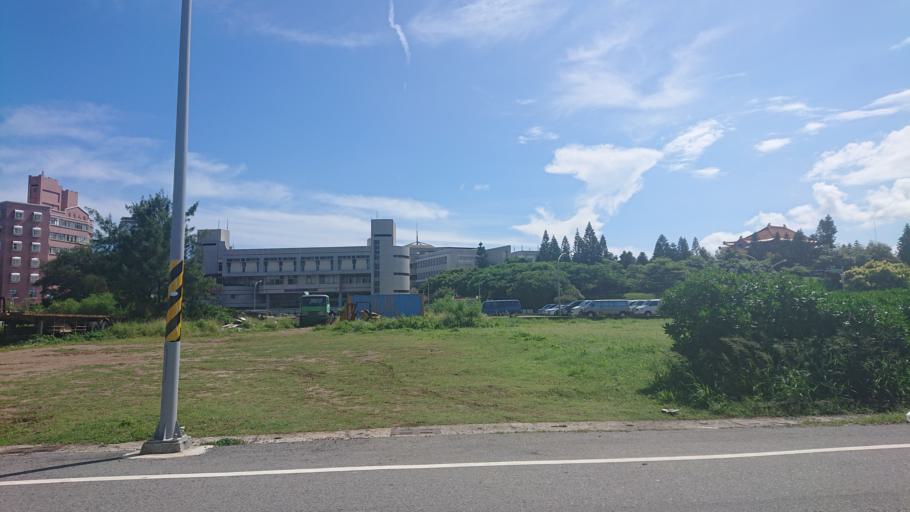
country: TW
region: Taiwan
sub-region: Penghu
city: Ma-kung
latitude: 23.5691
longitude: 119.5753
